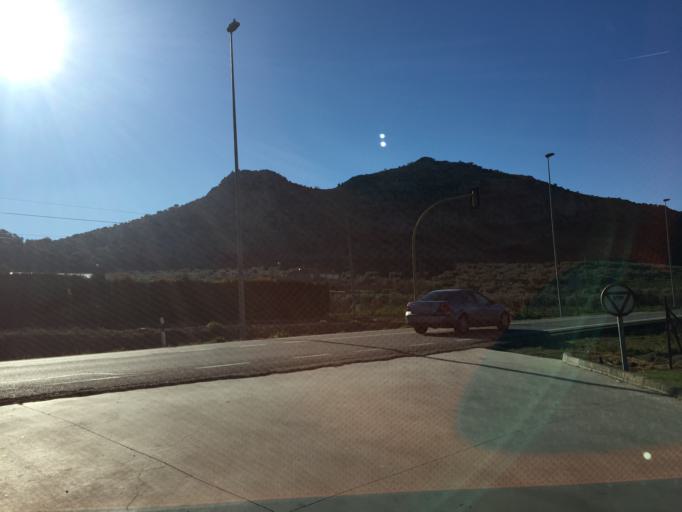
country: ES
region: Andalusia
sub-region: Provincia de Malaga
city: Cuevas del Becerro
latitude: 36.8704
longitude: -5.0505
